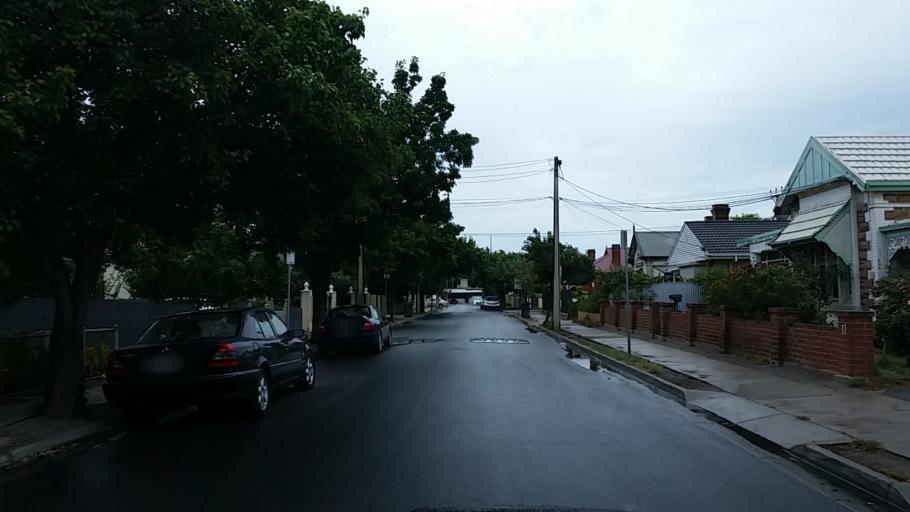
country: AU
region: South Australia
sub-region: City of West Torrens
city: Thebarton
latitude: -34.9258
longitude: 138.5610
